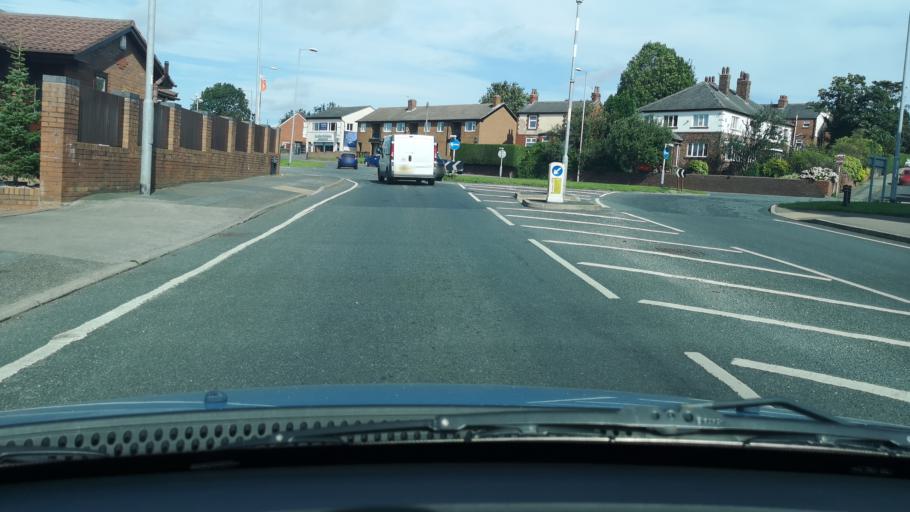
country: GB
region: England
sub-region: City and Borough of Wakefield
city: Ossett
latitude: 53.6909
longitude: -1.5893
